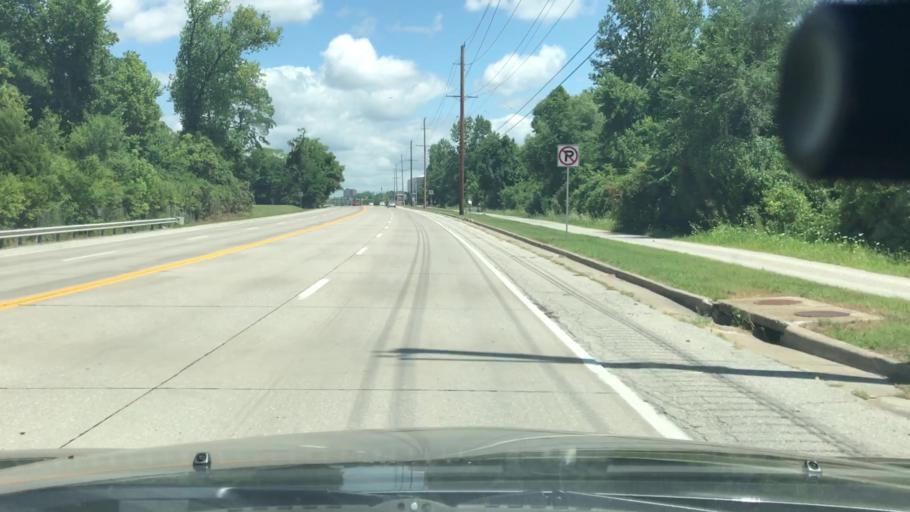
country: US
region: Missouri
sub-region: Saint Charles County
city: Saint Charles
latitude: 38.7447
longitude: -90.5146
